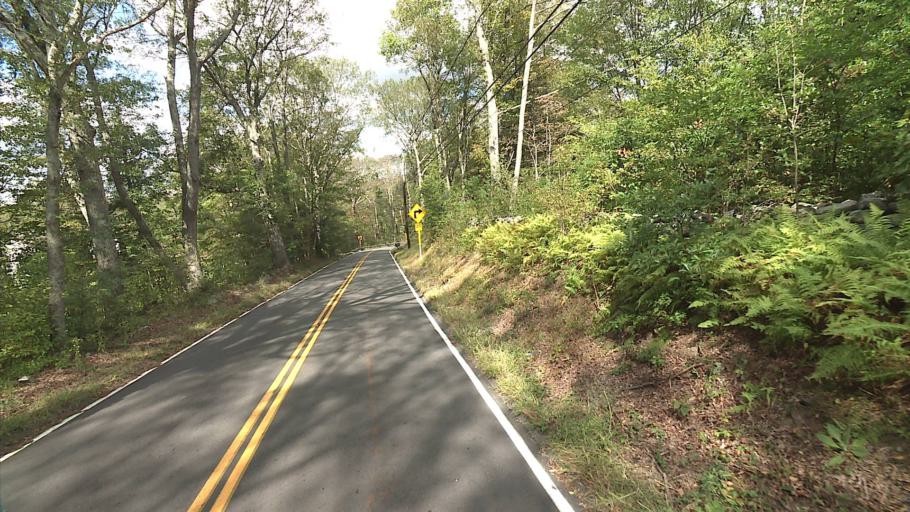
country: US
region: Connecticut
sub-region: Middlesex County
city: Higganum
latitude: 41.3964
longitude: -72.6044
